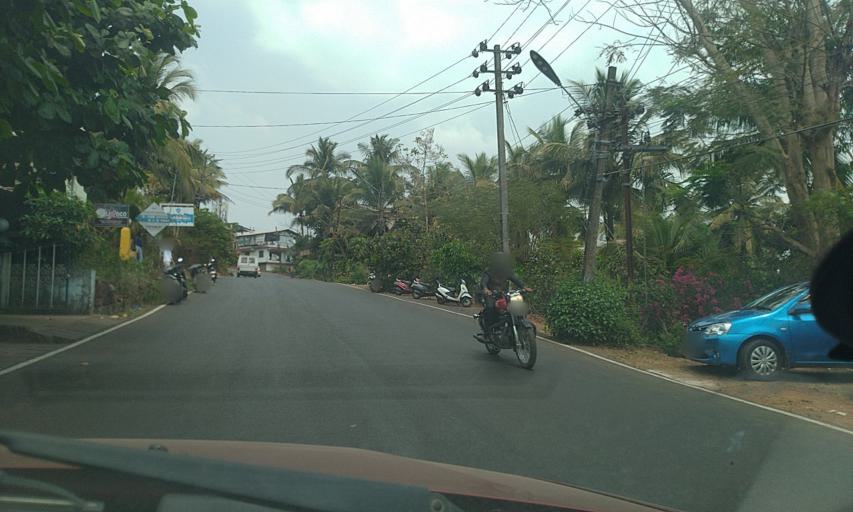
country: IN
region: Goa
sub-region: North Goa
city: Mapuca
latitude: 15.5998
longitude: 73.8089
